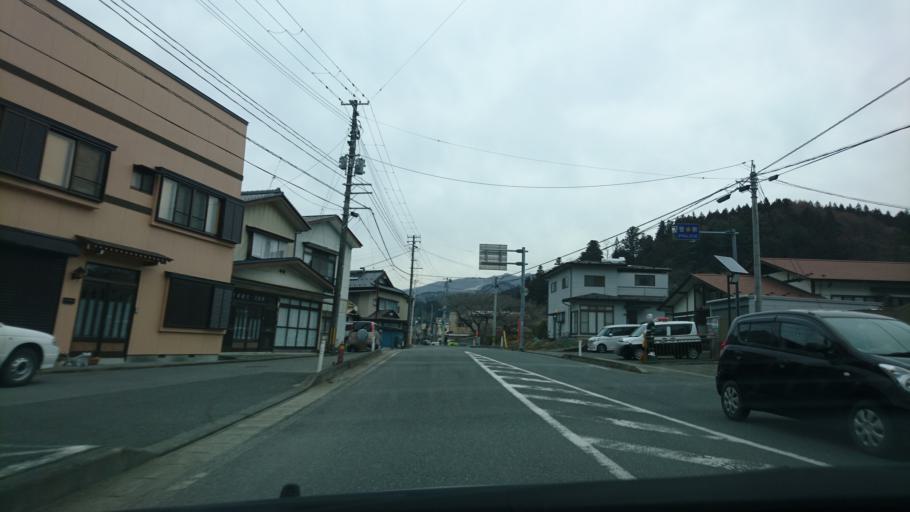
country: JP
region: Iwate
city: Ofunato
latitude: 39.1368
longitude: 141.5772
